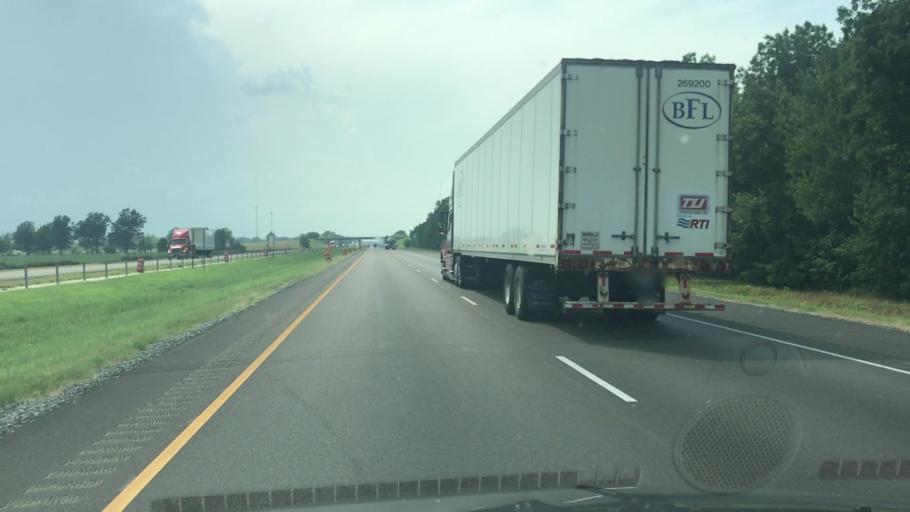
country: US
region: Arkansas
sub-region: Crittenden County
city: Earle
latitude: 35.1337
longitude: -90.4597
